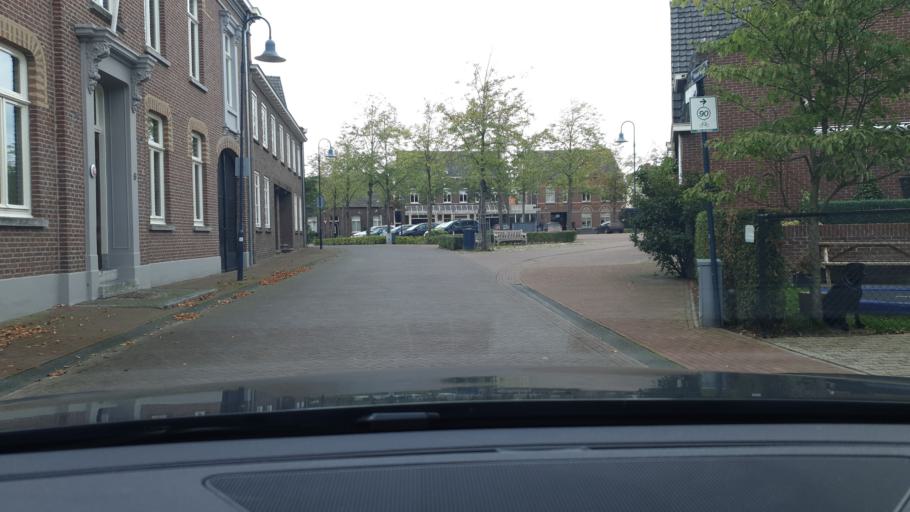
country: NL
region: Limburg
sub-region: Gemeente Venlo
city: Arcen
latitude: 51.4606
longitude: 6.1634
